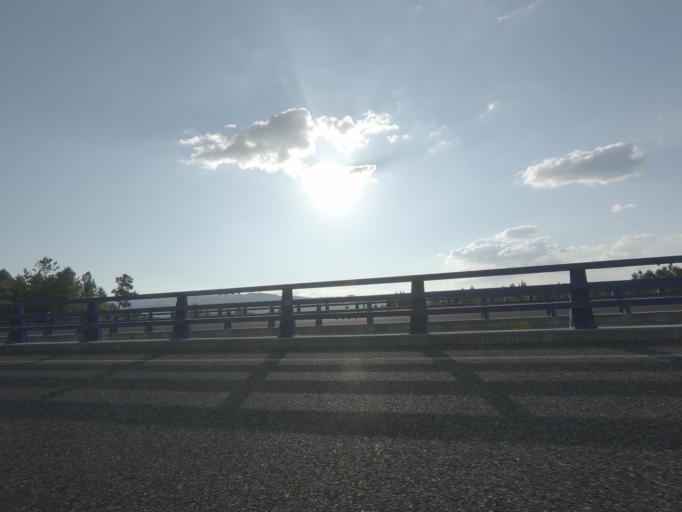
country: ES
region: Galicia
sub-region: Provincia de Ourense
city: Oimbra
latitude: 41.8745
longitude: -7.4319
